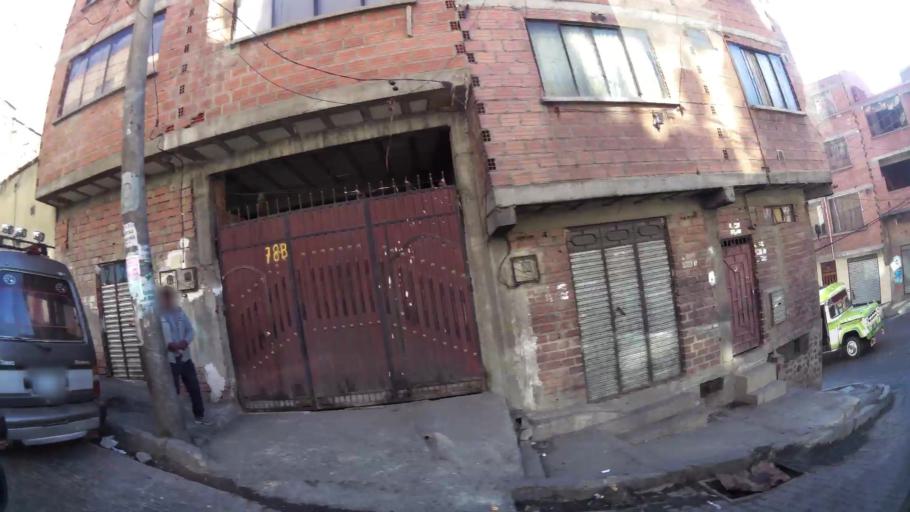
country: BO
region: La Paz
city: La Paz
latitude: -16.5056
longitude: -68.1519
